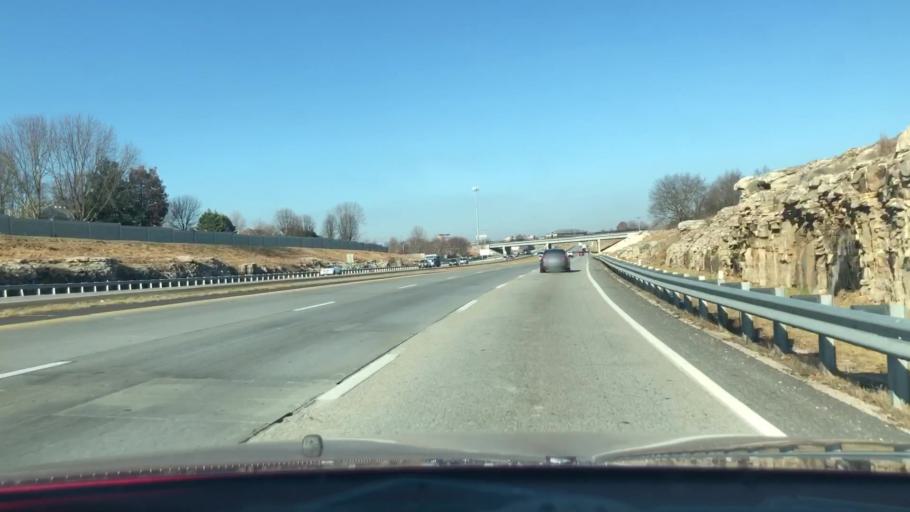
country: US
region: Missouri
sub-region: Greene County
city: Battlefield
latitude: 37.1359
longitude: -93.3067
